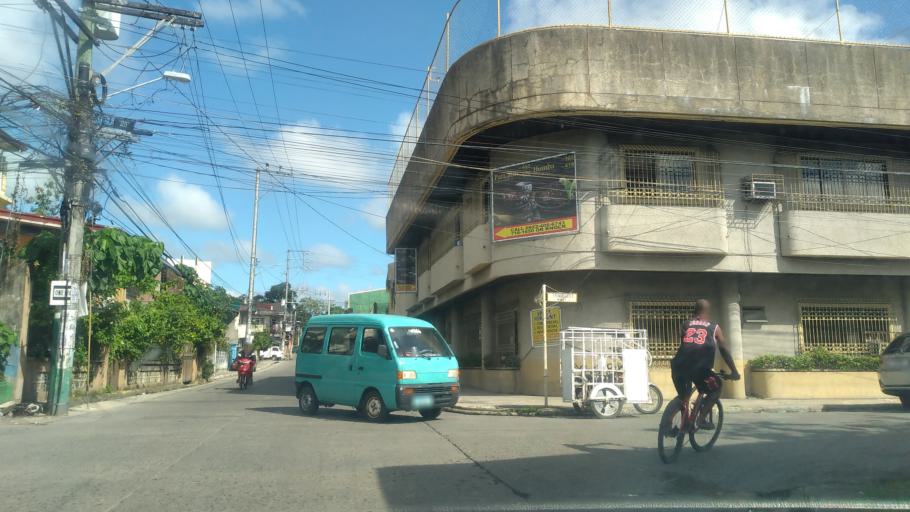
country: PH
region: Calabarzon
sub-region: Province of Quezon
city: Lucena
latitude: 13.9390
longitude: 121.6119
